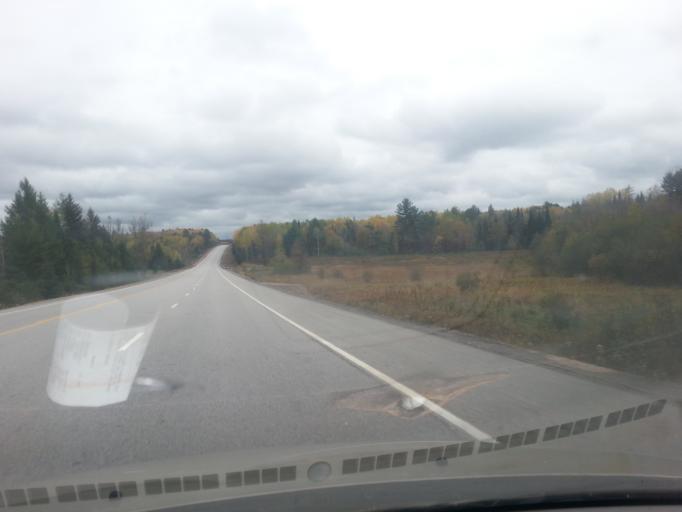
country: CA
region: Ontario
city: Mattawa
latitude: 46.2800
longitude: -78.4334
